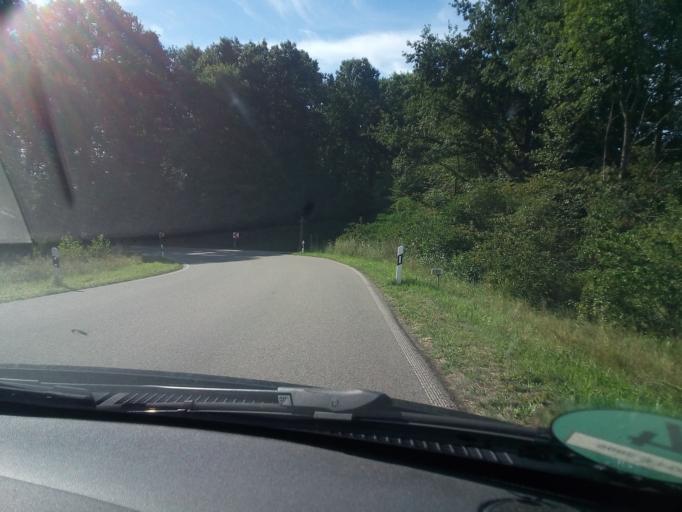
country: DE
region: Baden-Wuerttemberg
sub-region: Freiburg Region
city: Achern
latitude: 48.6544
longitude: 8.0564
